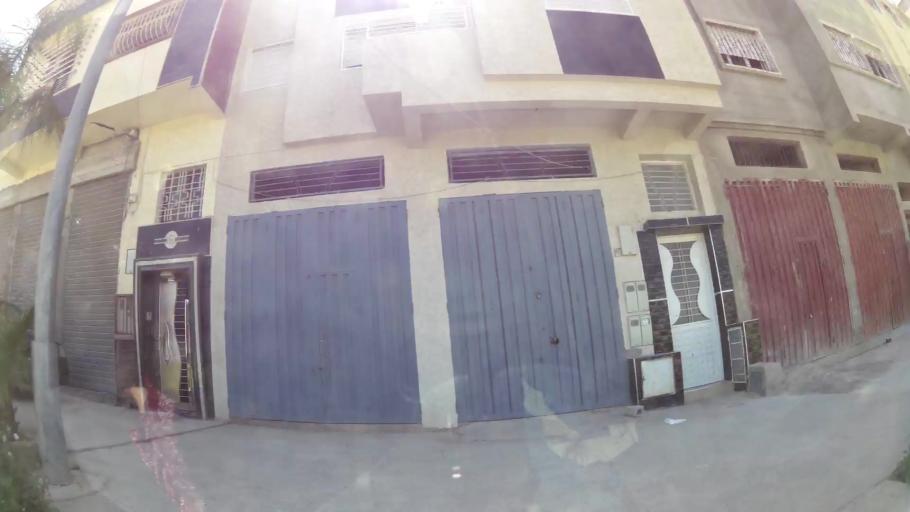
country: MA
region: Fes-Boulemane
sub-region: Fes
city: Fes
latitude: 34.0242
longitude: -5.0437
